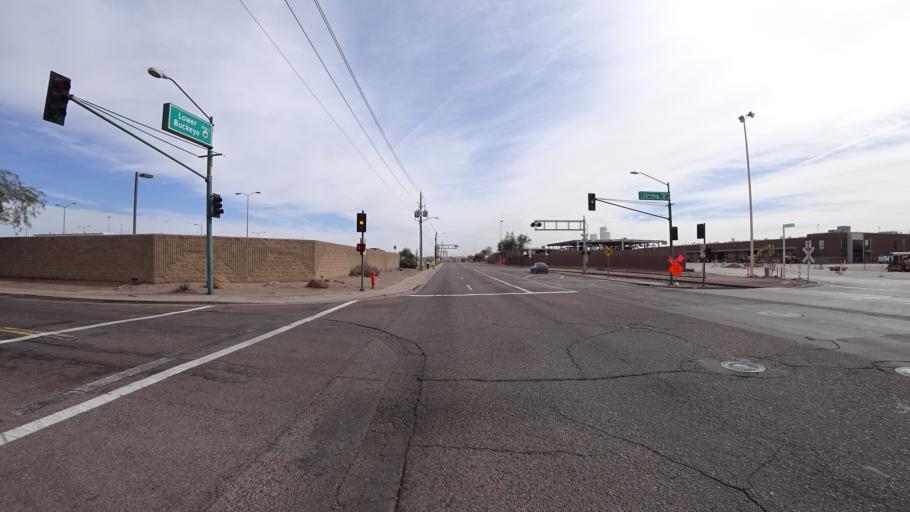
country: US
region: Arizona
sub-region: Maricopa County
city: Phoenix
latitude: 33.4223
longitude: -112.1062
